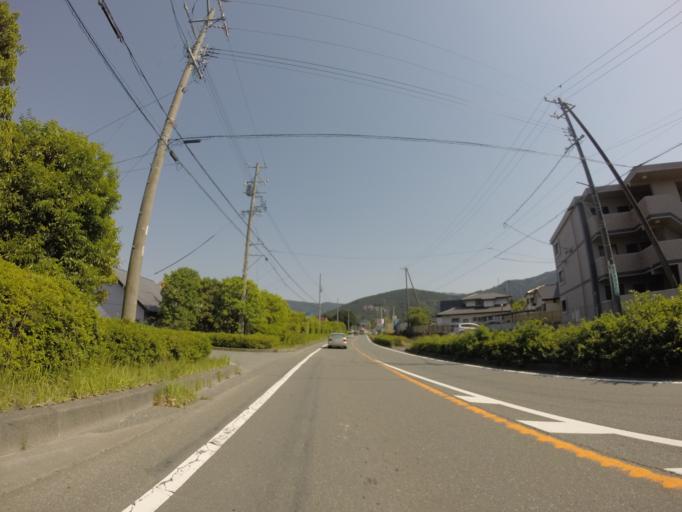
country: JP
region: Shizuoka
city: Fujinomiya
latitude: 35.1921
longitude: 138.5899
